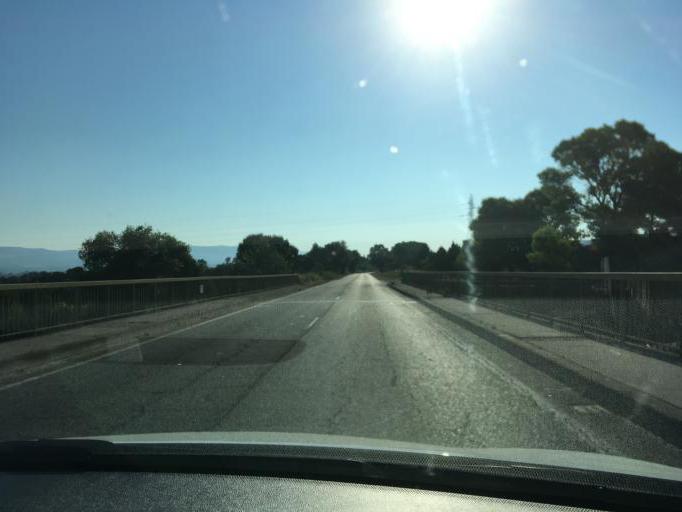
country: FR
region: Provence-Alpes-Cote d'Azur
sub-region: Departement des Bouches-du-Rhone
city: Mallemort
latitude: 43.7147
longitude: 5.2046
